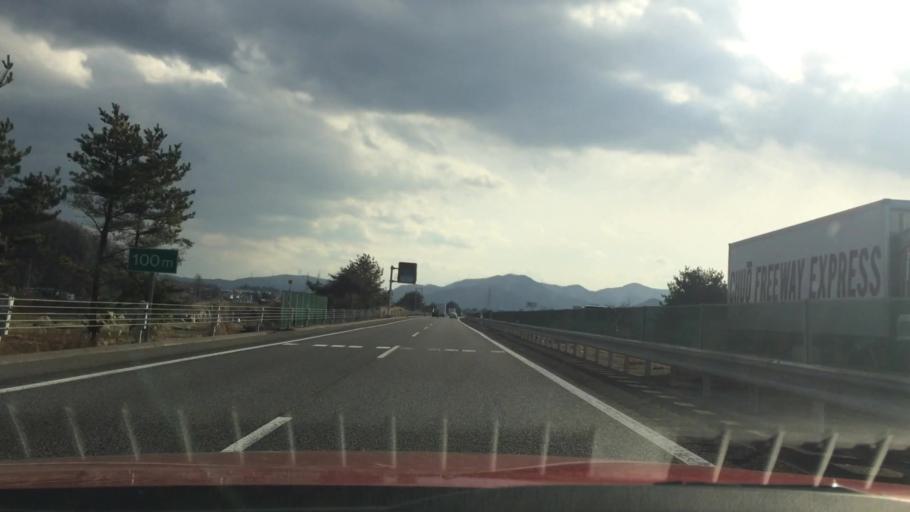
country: JP
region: Nagano
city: Shiojiri
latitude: 36.1542
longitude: 137.9681
